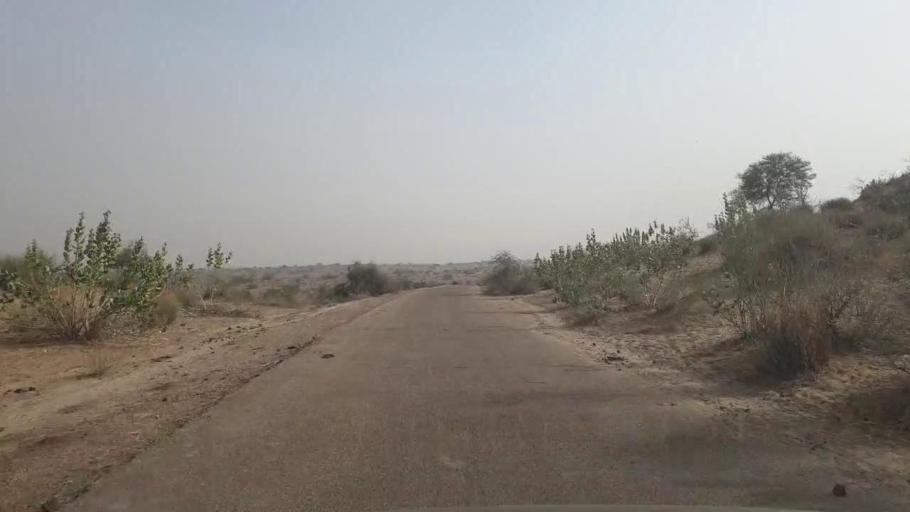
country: PK
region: Sindh
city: Chor
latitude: 25.5065
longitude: 69.9692
